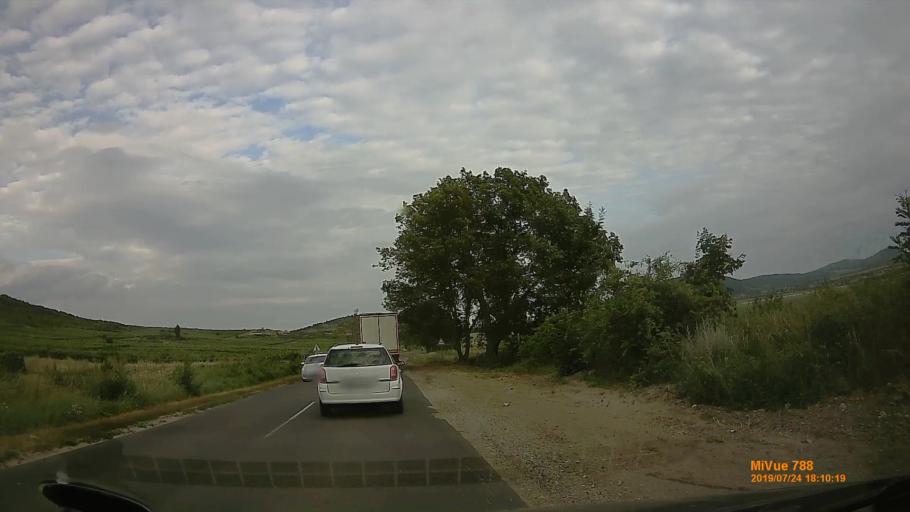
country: HU
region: Borsod-Abauj-Zemplen
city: Abaujszanto
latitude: 48.2614
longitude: 21.1880
